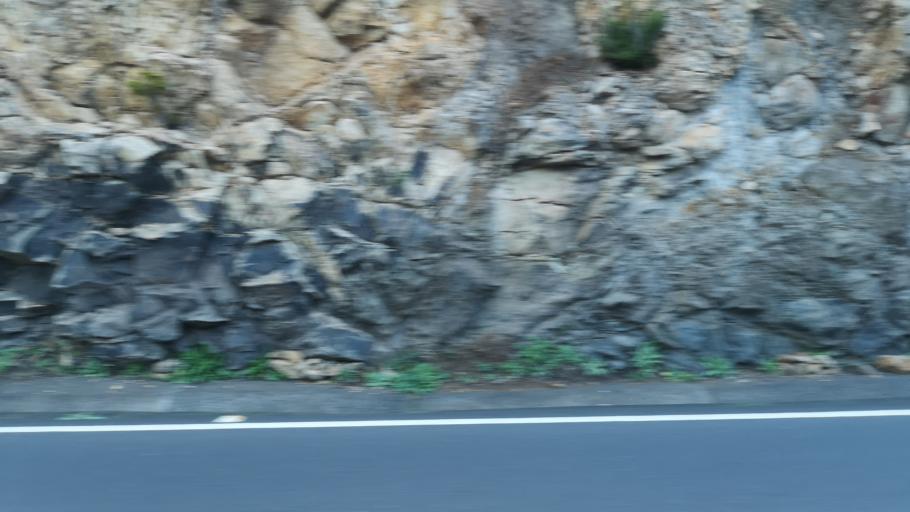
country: ES
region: Canary Islands
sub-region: Provincia de Santa Cruz de Tenerife
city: Alajero
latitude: 28.0986
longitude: -17.1971
